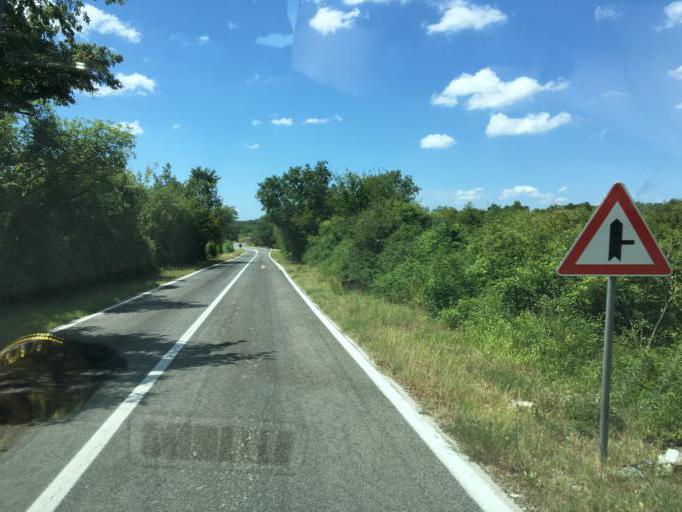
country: HR
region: Istarska
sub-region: Grad Rovinj
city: Rovinj
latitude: 45.1408
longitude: 13.7253
